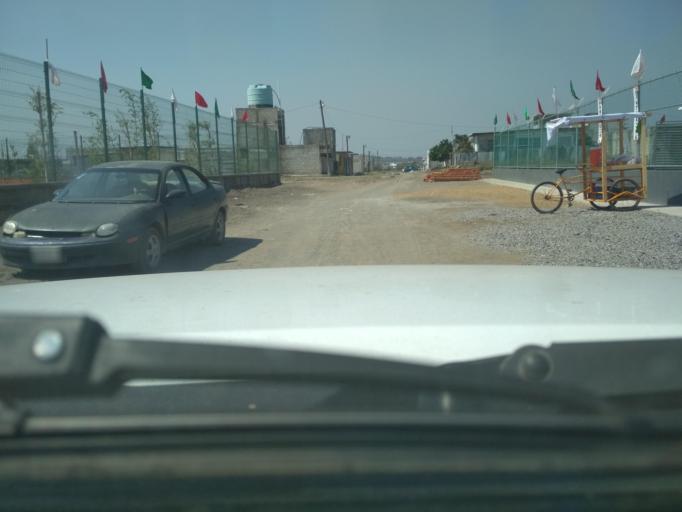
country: MX
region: Veracruz
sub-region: Veracruz
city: Lomas de Rio Medio Cuatro
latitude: 19.1932
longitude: -96.1990
